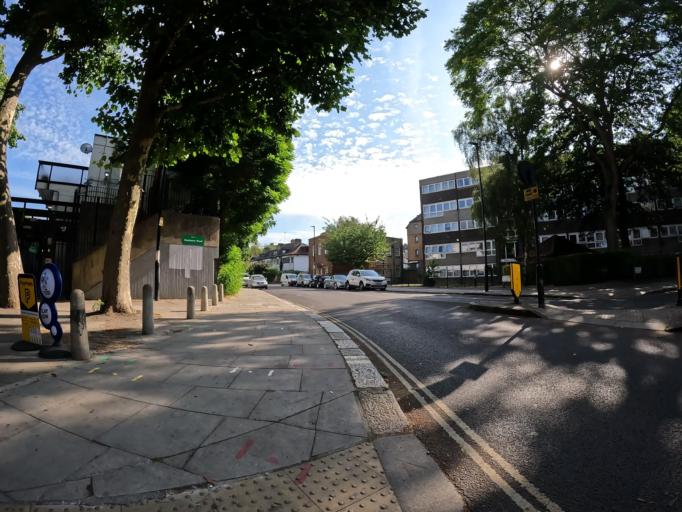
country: GB
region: England
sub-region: Greater London
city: Belsize Park
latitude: 51.5646
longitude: -0.1739
